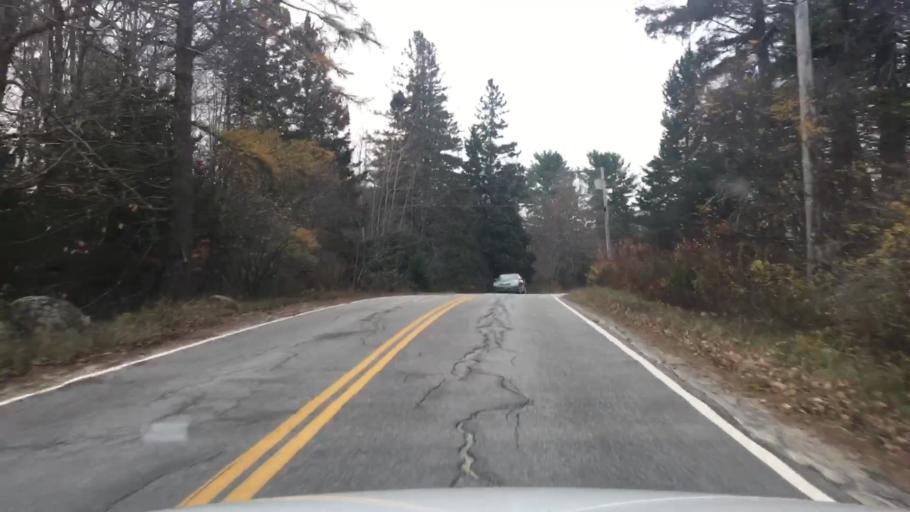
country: US
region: Maine
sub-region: Hancock County
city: Sedgwick
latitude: 44.2917
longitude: -68.5550
